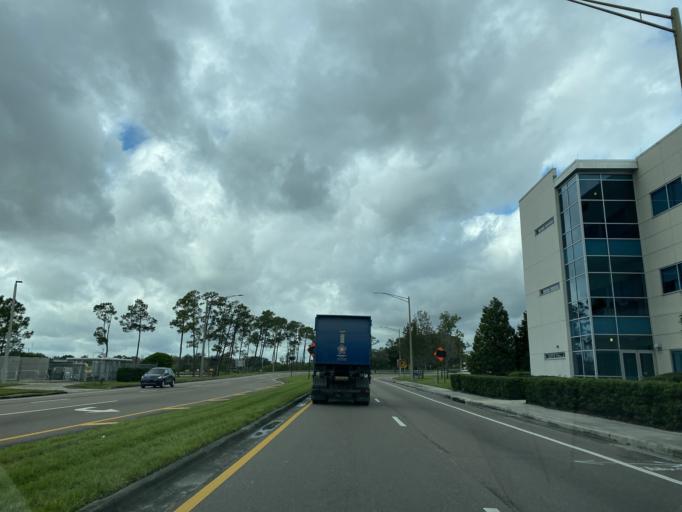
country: US
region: Florida
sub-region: Orange County
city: Belle Isle
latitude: 28.4420
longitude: -81.3025
